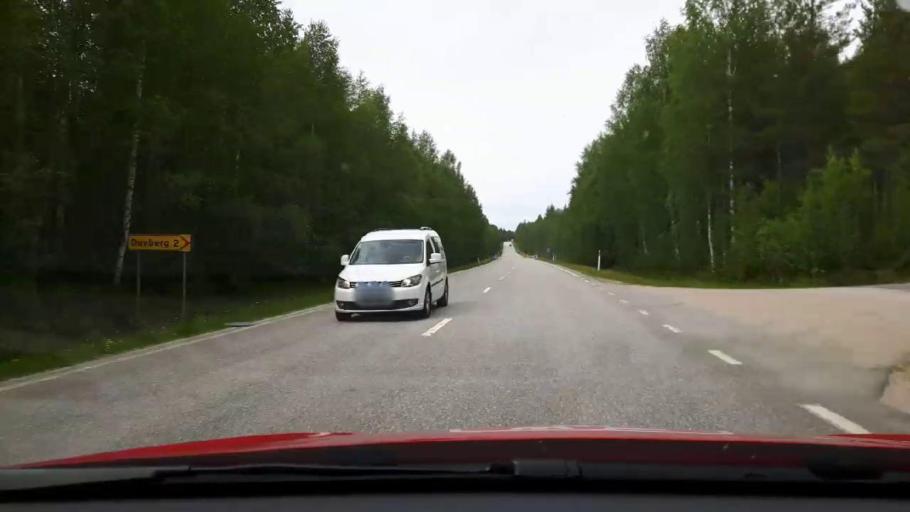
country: SE
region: Jaemtland
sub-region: Harjedalens Kommun
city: Sveg
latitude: 62.0980
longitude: 14.2272
